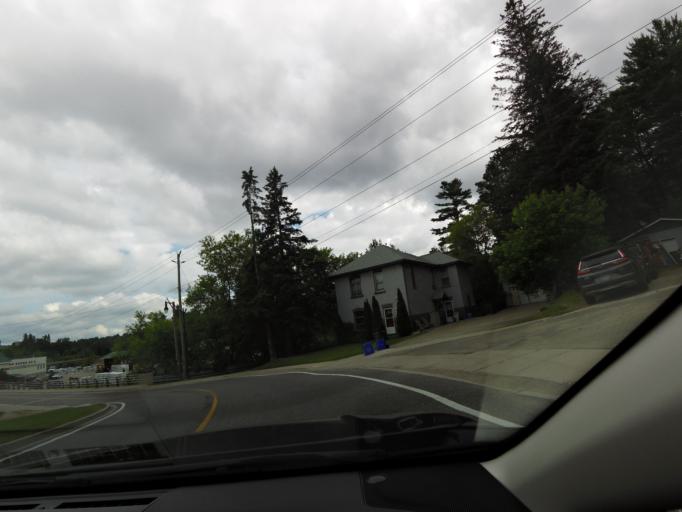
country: CA
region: Ontario
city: Bracebridge
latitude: 45.0396
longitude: -79.3063
